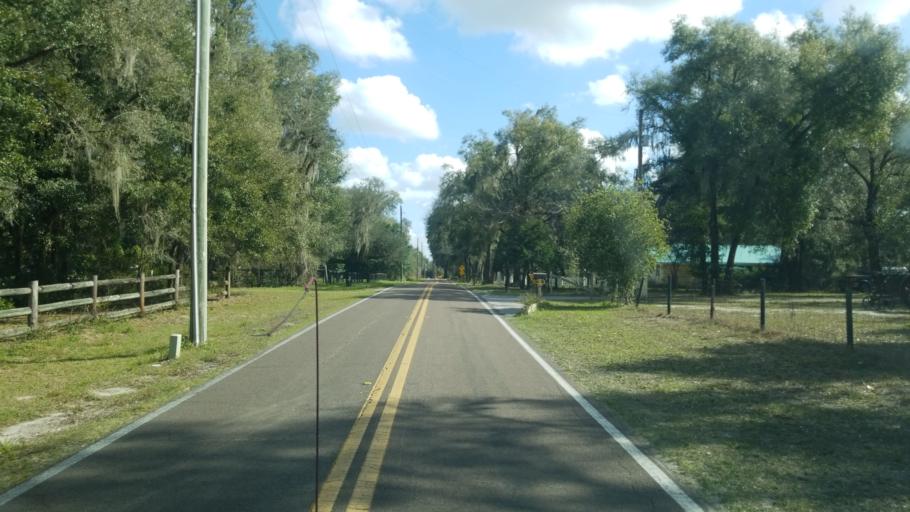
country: US
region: Florida
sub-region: Citrus County
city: Floral City
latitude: 28.7517
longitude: -82.2568
